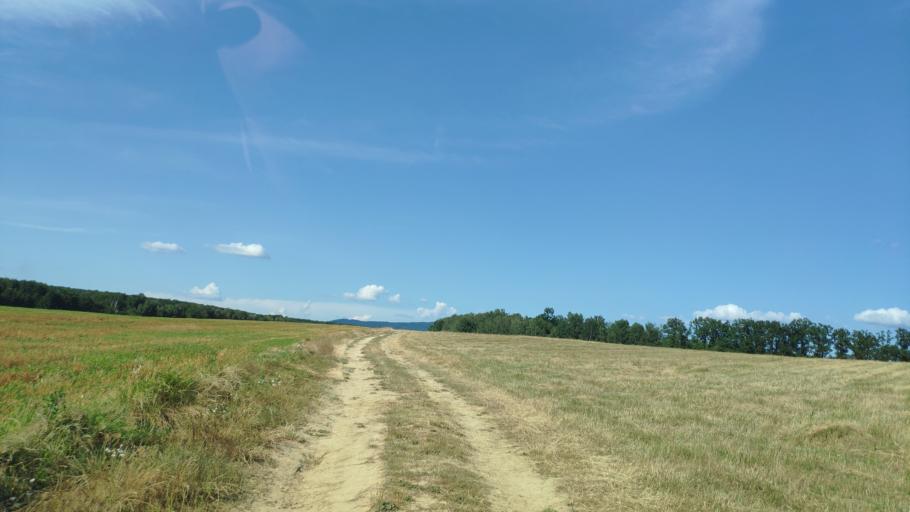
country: SK
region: Presovsky
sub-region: Okres Presov
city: Presov
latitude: 48.9091
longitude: 21.2926
